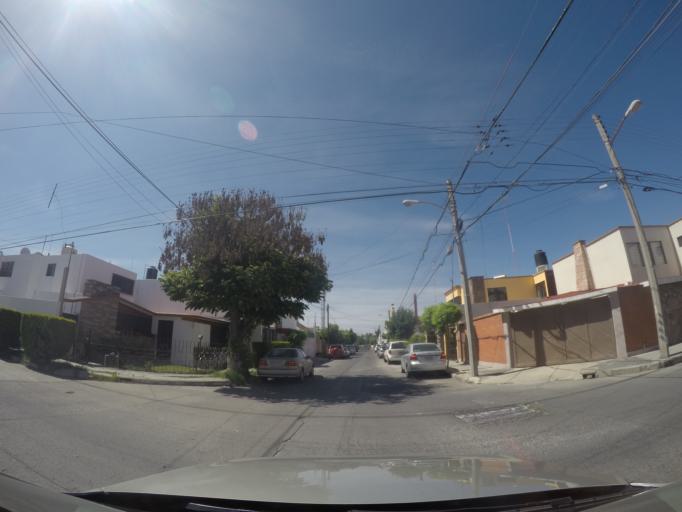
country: MX
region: San Luis Potosi
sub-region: San Luis Potosi
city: San Luis Potosi
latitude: 22.1523
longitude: -101.0077
